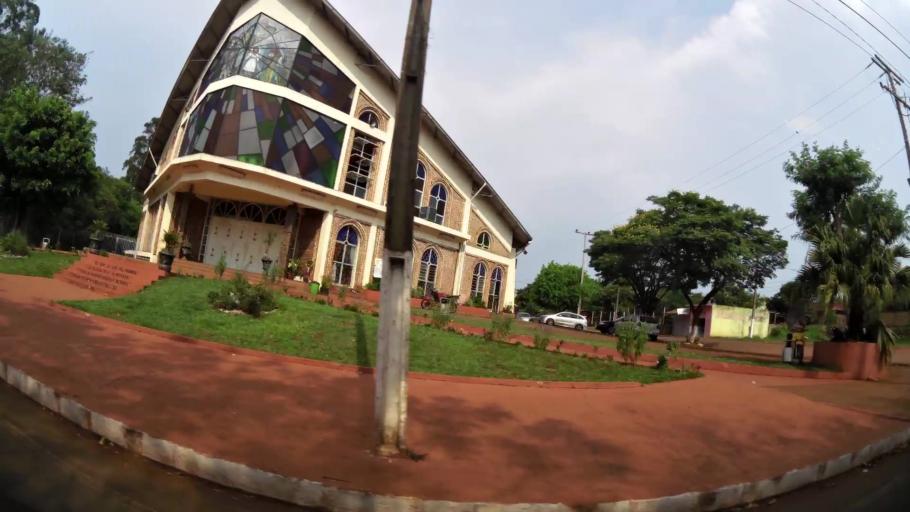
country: PY
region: Alto Parana
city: Ciudad del Este
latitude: -25.4933
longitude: -54.6490
